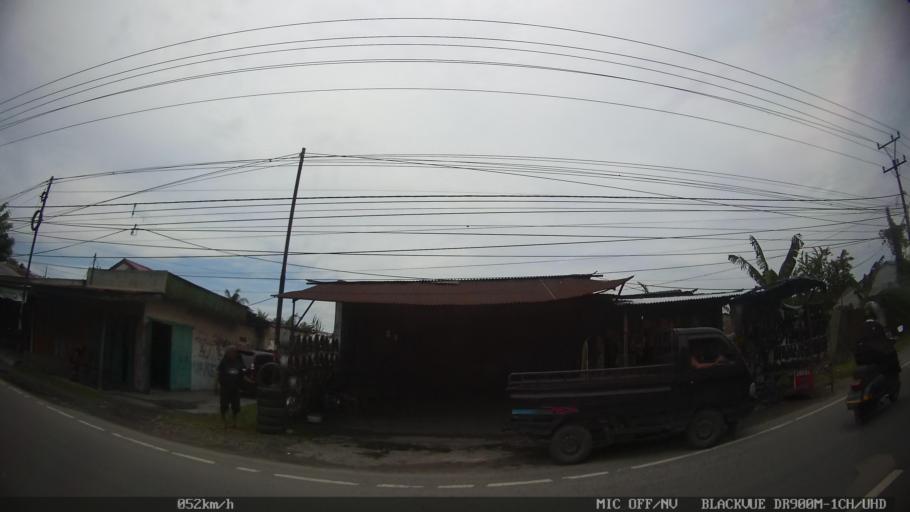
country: ID
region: North Sumatra
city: Sunggal
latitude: 3.5994
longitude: 98.5617
